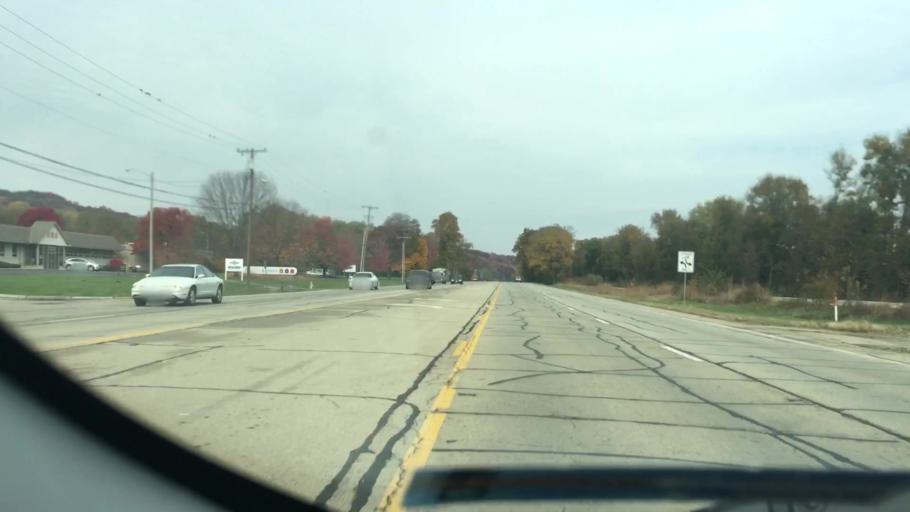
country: US
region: Illinois
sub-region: Peoria County
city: Peoria Heights
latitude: 40.7656
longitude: -89.5695
